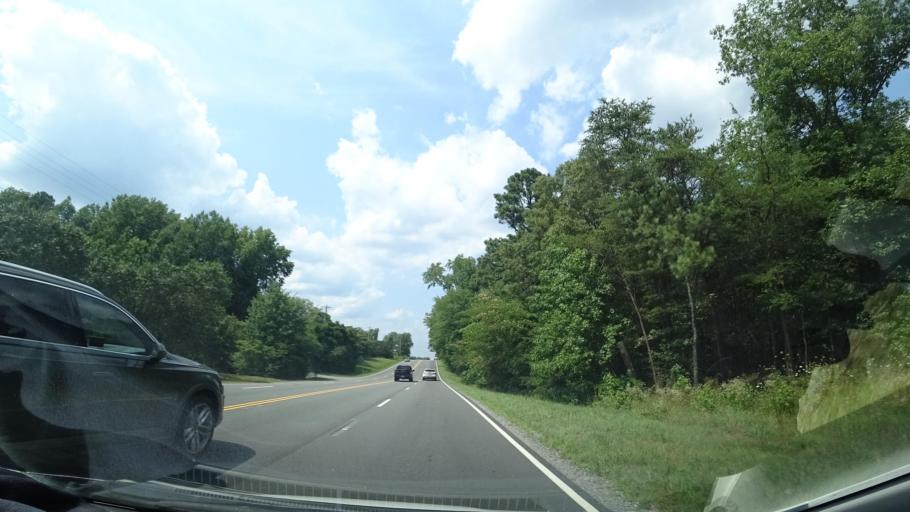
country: US
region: Virginia
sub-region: Hanover County
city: Ashland
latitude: 37.8516
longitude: -77.4635
